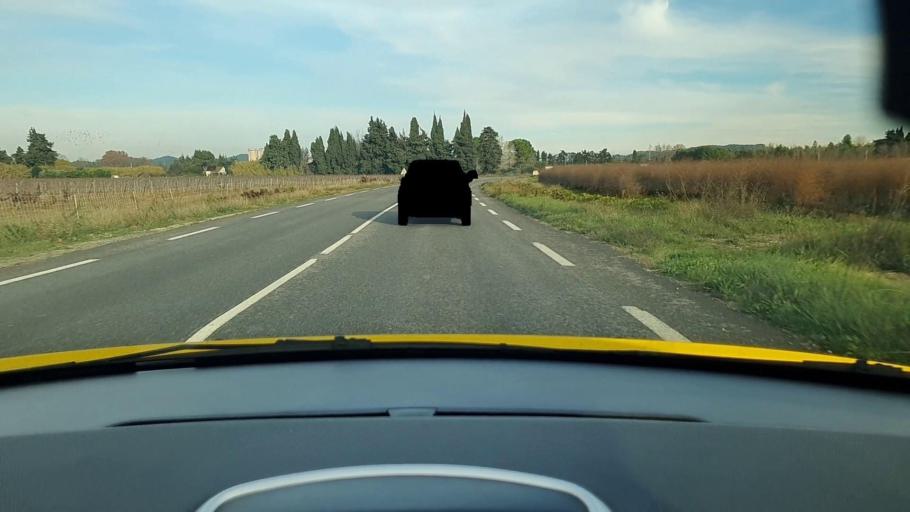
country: FR
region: Languedoc-Roussillon
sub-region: Departement du Gard
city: Beaucaire
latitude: 43.7877
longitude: 4.6276
